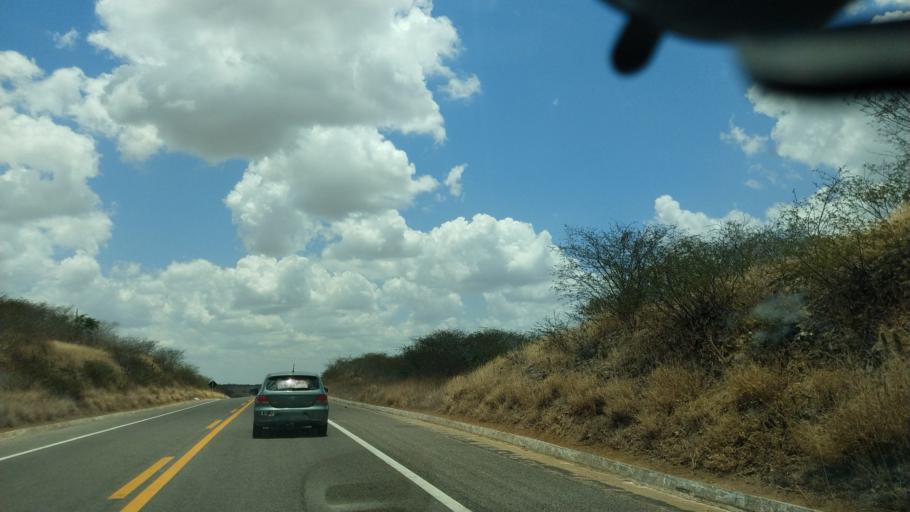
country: BR
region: Rio Grande do Norte
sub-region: Cerro Cora
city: Cerro Cora
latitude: -6.2090
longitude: -36.2920
